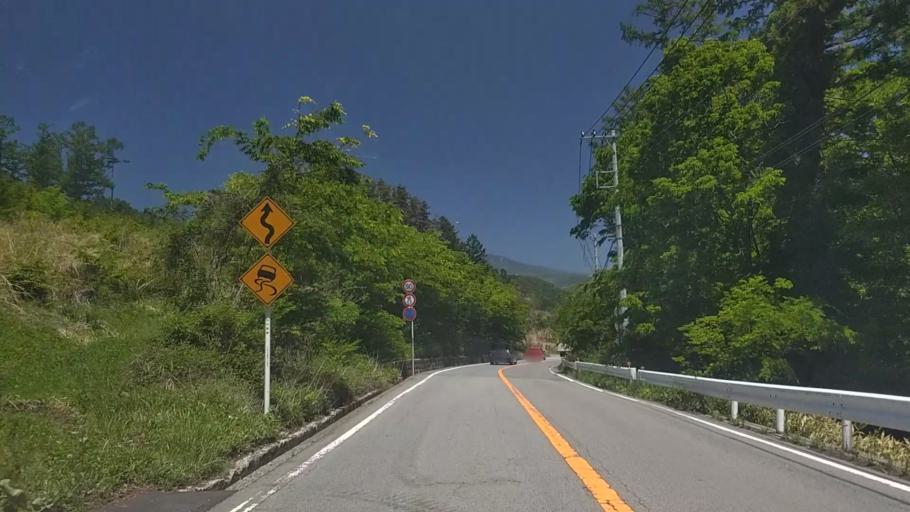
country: JP
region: Yamanashi
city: Nirasaki
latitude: 35.8576
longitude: 138.4304
